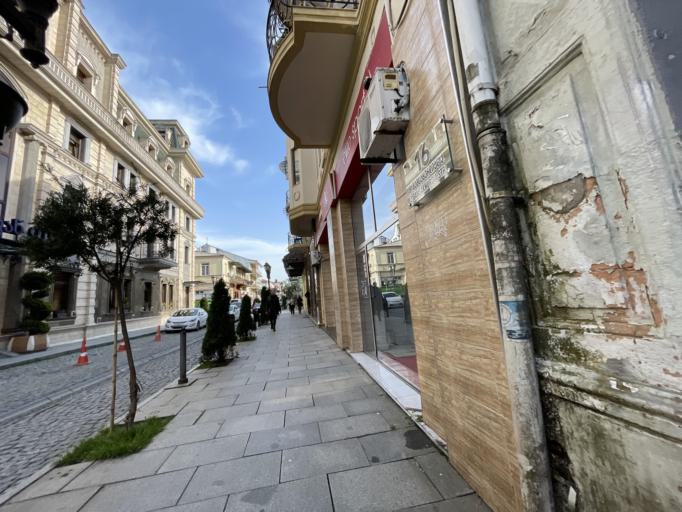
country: GE
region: Ajaria
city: Batumi
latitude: 41.6511
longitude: 41.6410
